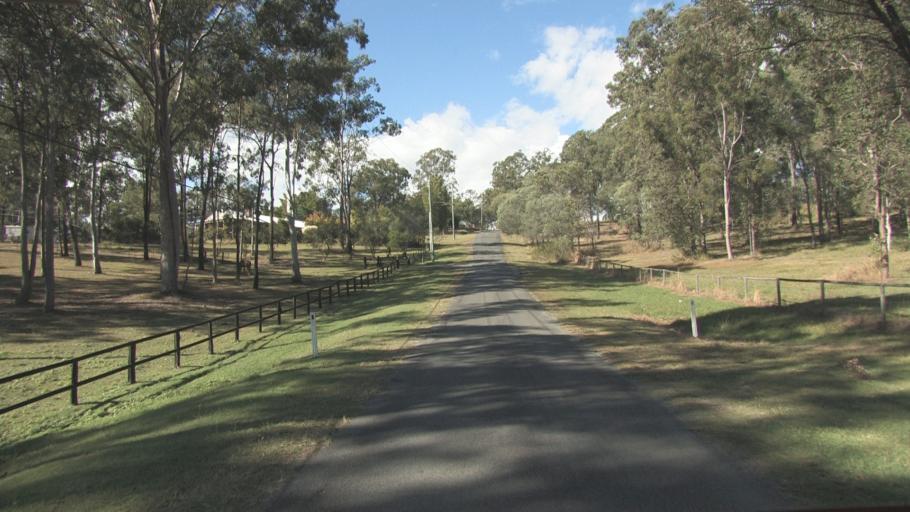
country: AU
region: Queensland
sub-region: Logan
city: Chambers Flat
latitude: -27.8099
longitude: 153.0867
